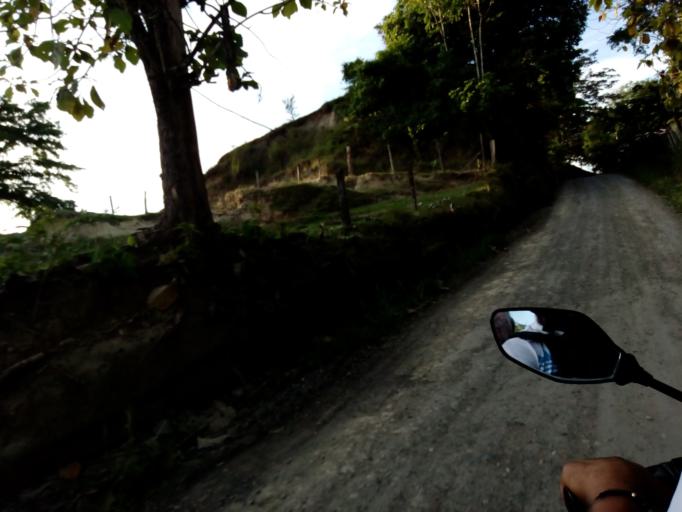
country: CO
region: Boyaca
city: Puerto Boyaca
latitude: 5.9627
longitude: -74.5905
